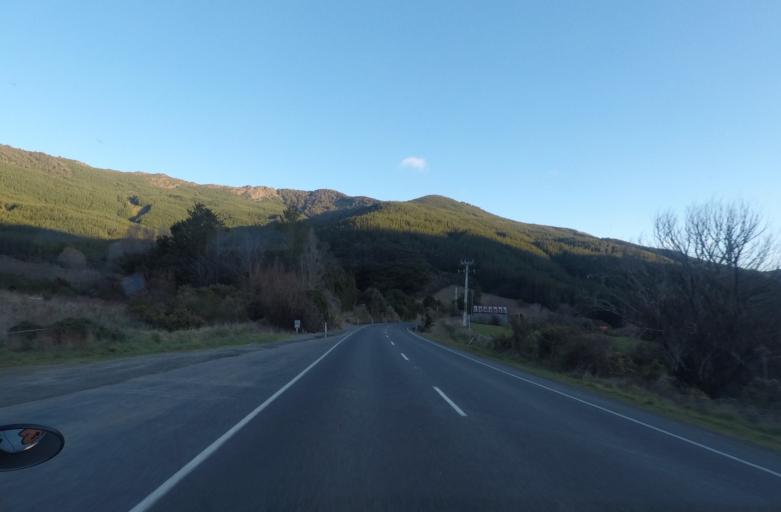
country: NZ
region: Marlborough
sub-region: Marlborough District
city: Picton
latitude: -41.2806
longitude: 173.7275
